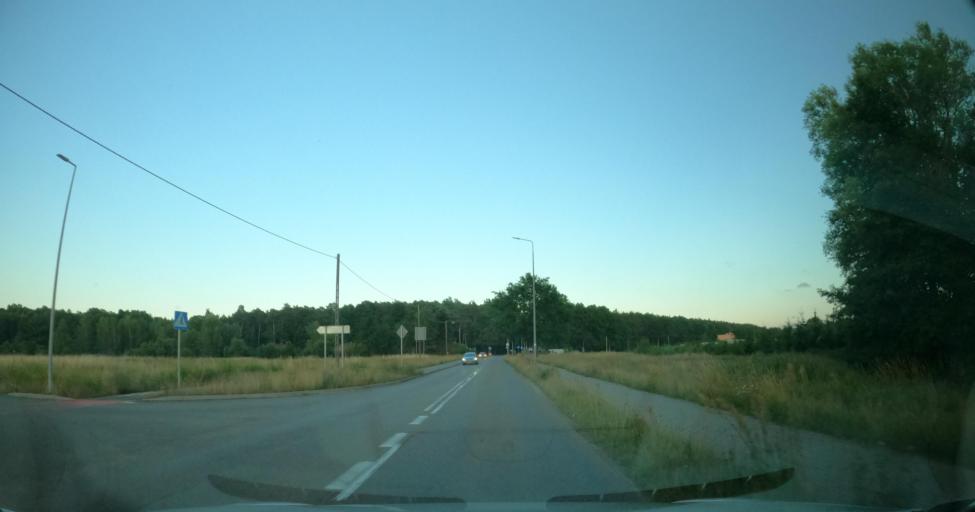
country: PL
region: Pomeranian Voivodeship
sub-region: Powiat leborski
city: Lebork
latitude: 54.5268
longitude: 17.7717
